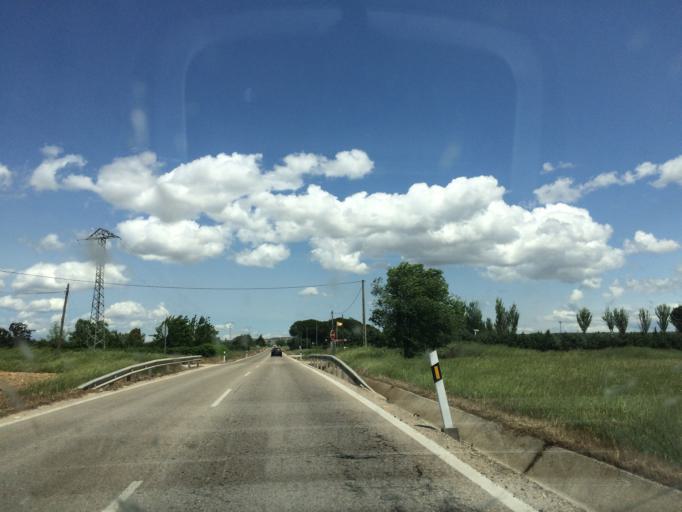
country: ES
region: Madrid
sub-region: Provincia de Madrid
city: Fuente el Saz
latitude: 40.6501
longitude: -3.4991
